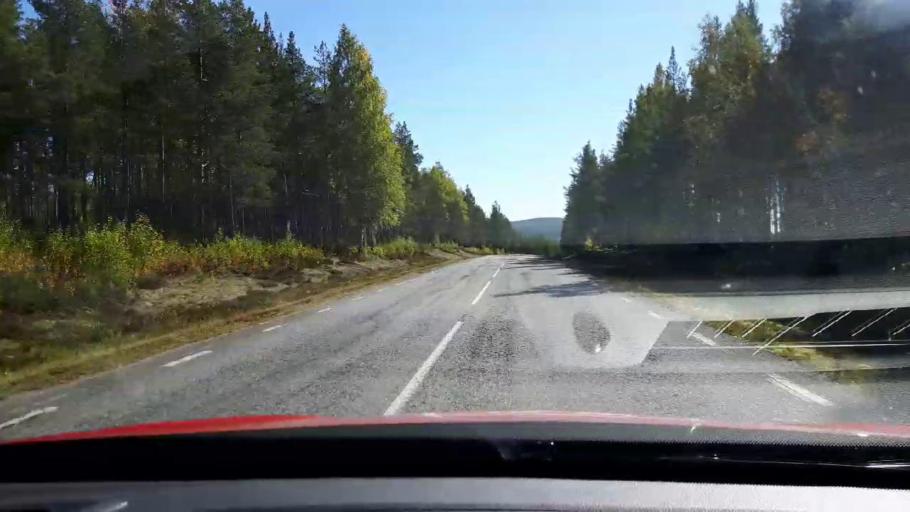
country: SE
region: Jaemtland
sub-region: Harjedalens Kommun
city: Sveg
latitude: 62.2983
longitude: 14.0708
